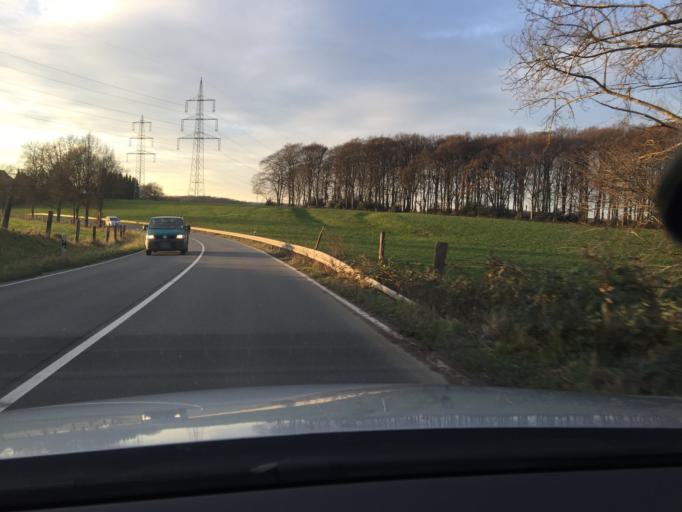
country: DE
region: North Rhine-Westphalia
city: Sprockhovel
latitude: 51.3245
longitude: 7.2442
